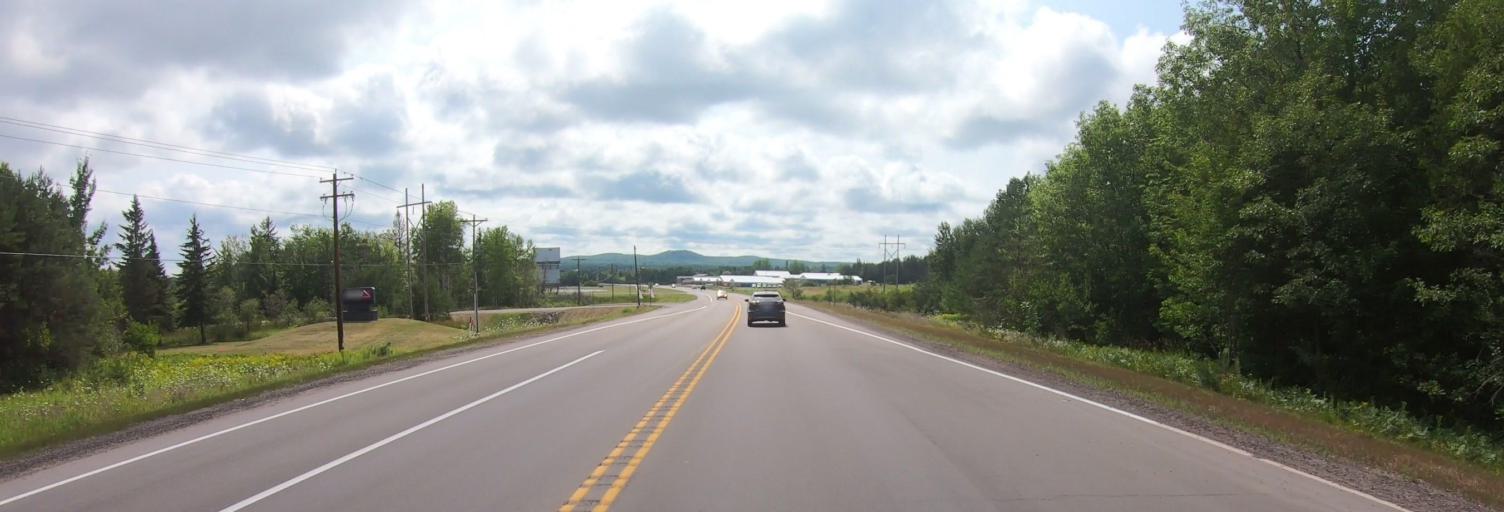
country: US
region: Michigan
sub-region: Houghton County
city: Hancock
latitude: 47.0978
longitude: -88.6158
